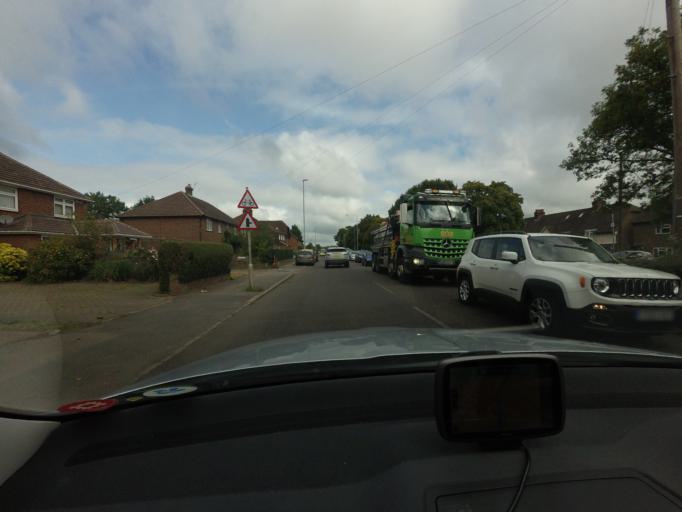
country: GB
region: England
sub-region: Kent
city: Tonbridge
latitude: 51.2107
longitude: 0.2793
